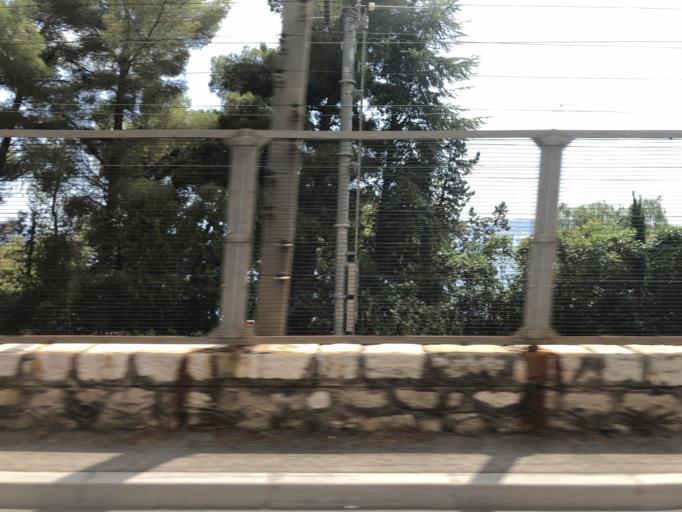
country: FR
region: Provence-Alpes-Cote d'Azur
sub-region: Departement des Alpes-Maritimes
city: Eze
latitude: 43.7227
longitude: 7.3640
